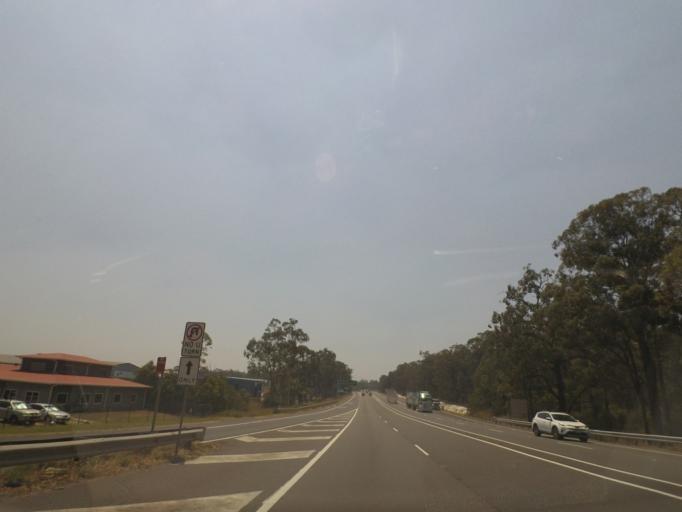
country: AU
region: New South Wales
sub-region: Newcastle
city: Beresfield
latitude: -32.8117
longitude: 151.6410
